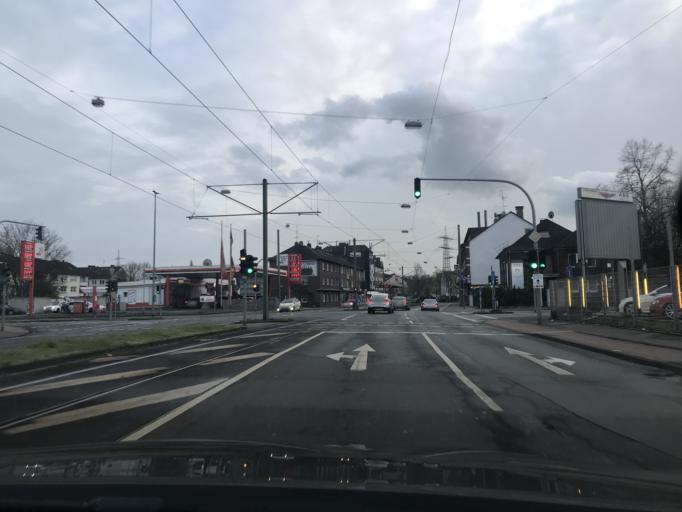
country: DE
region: North Rhine-Westphalia
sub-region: Regierungsbezirk Dusseldorf
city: Dinslaken
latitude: 51.5184
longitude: 6.7415
